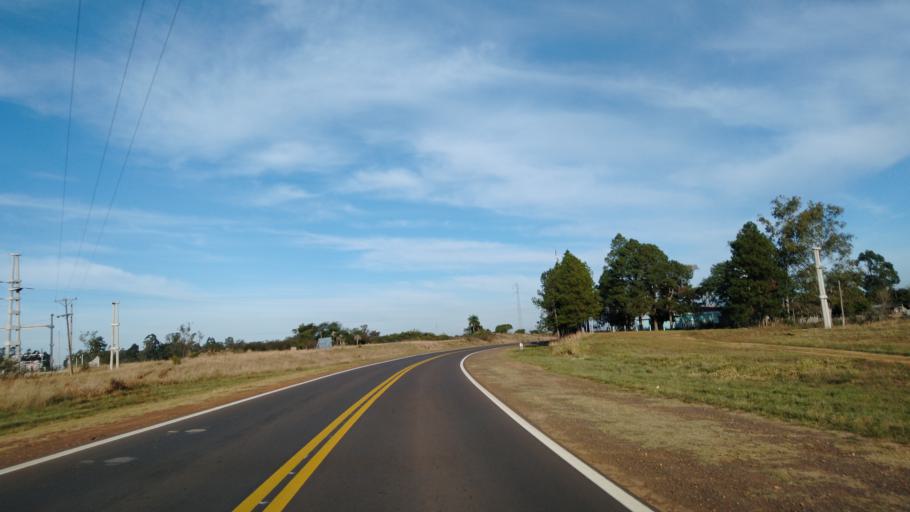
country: AR
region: Corrientes
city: Yapeyu
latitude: -29.4201
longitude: -56.8393
